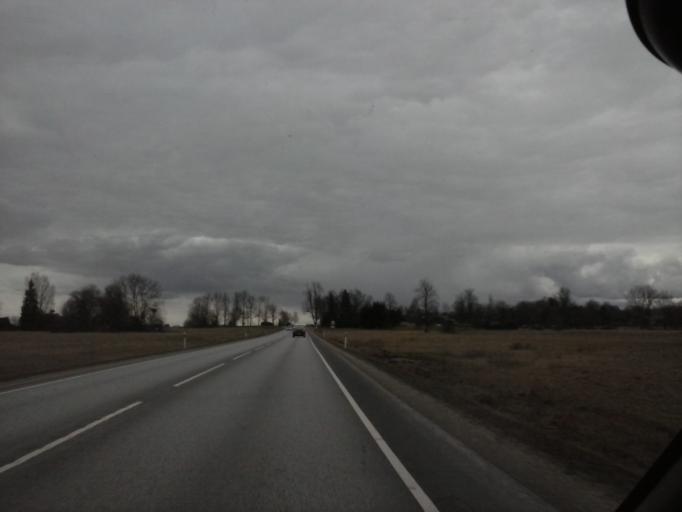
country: EE
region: Jaervamaa
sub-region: Paide linn
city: Paide
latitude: 58.8663
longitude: 25.7078
